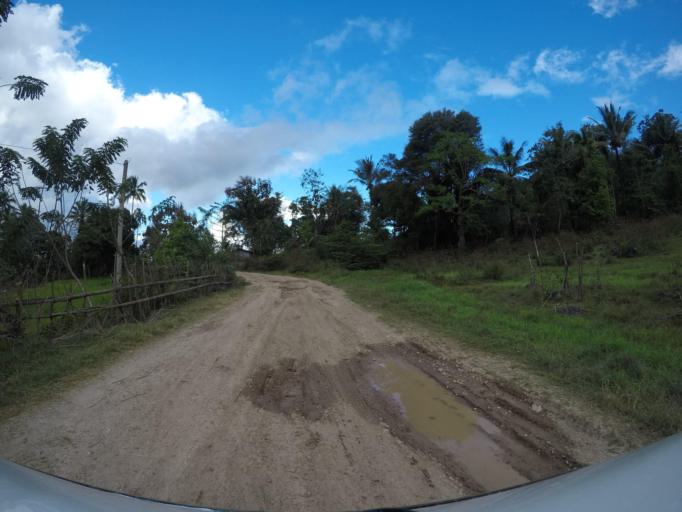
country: TL
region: Baucau
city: Venilale
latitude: -8.6842
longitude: 126.6527
